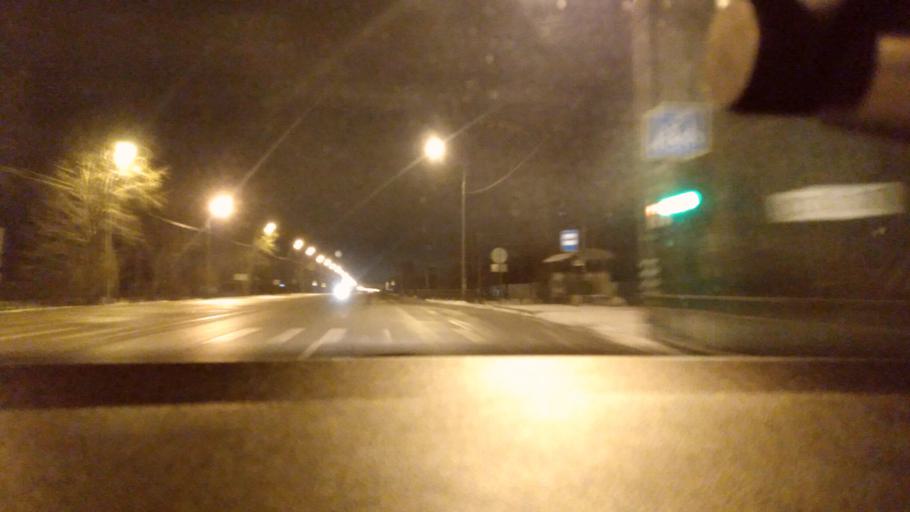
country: RU
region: Moskovskaya
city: Bronnitsy
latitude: 55.3862
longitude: 38.3462
